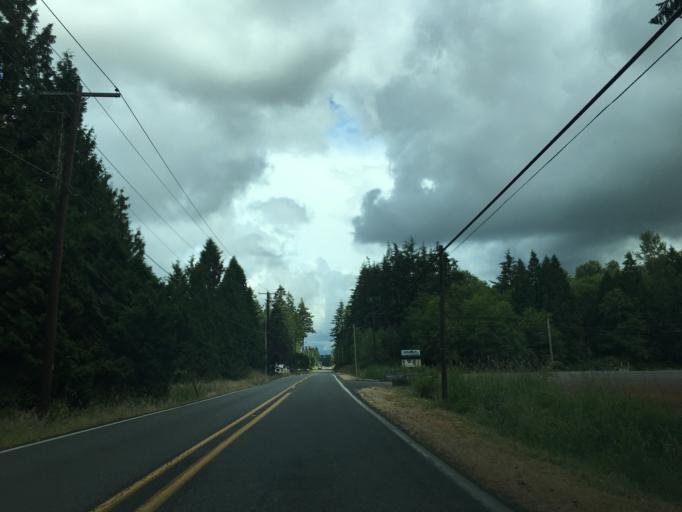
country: US
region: Washington
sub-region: Whatcom County
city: Blaine
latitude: 48.9584
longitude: -122.7300
